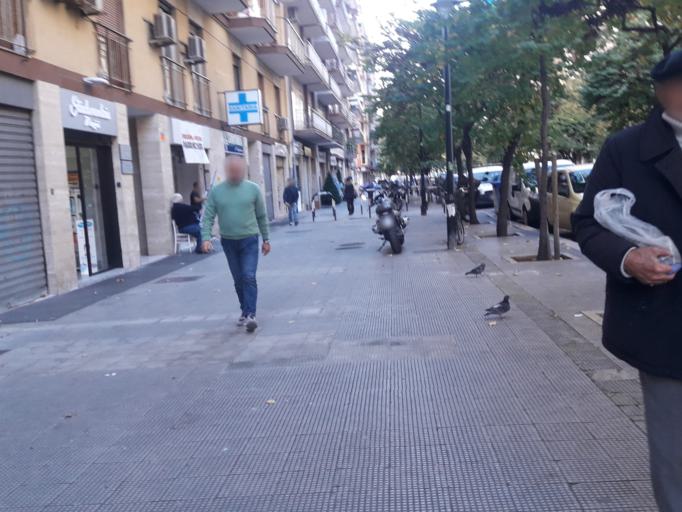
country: IT
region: Apulia
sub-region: Provincia di Bari
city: Bari
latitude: 41.1255
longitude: 16.8584
